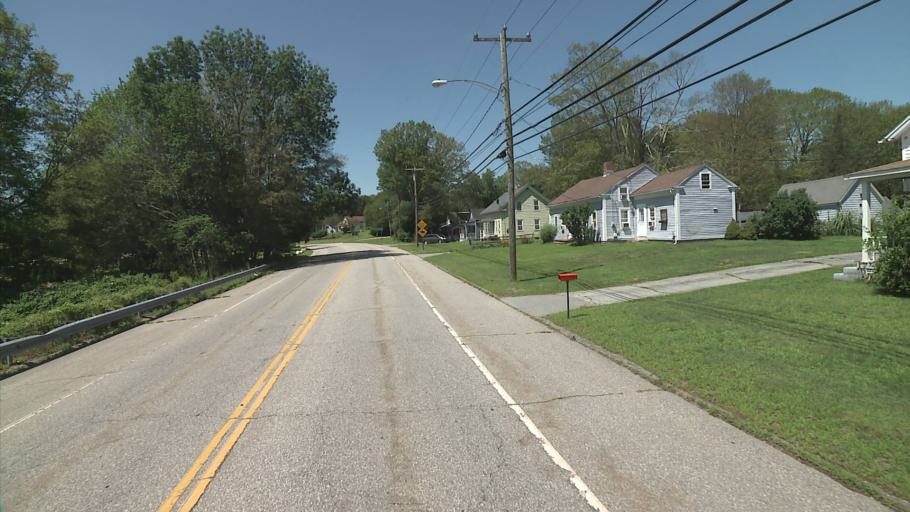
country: US
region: Connecticut
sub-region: Windham County
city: Wauregan
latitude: 41.7221
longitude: -71.9122
